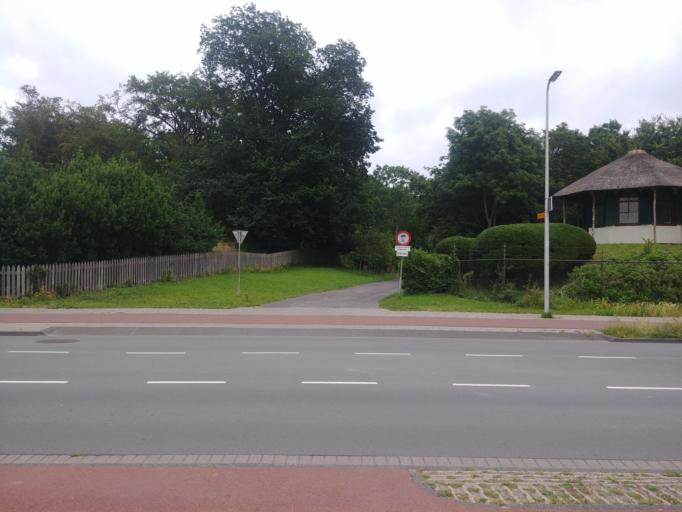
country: NL
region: North Holland
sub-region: Gemeente Bloemendaal
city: Bloemendaal
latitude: 52.4104
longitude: 4.6156
